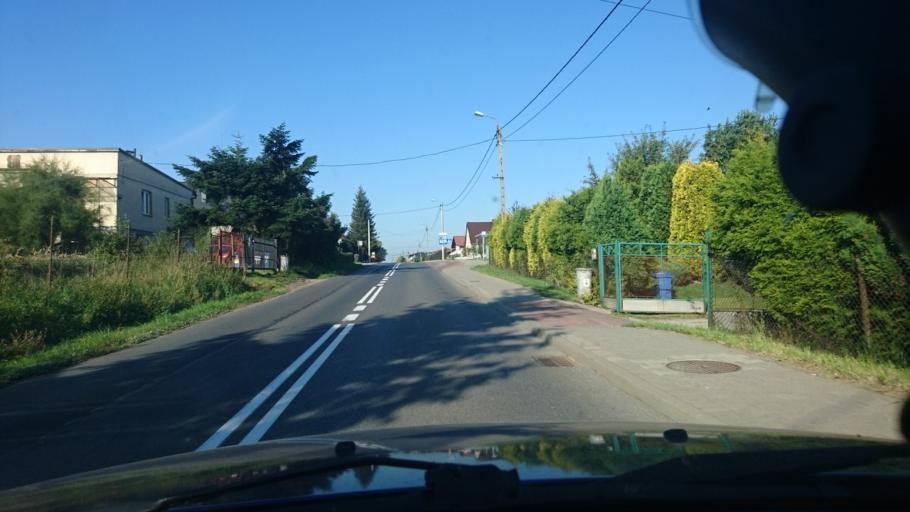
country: PL
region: Silesian Voivodeship
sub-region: Bielsko-Biala
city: Bielsko-Biala
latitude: 49.8508
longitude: 19.0603
